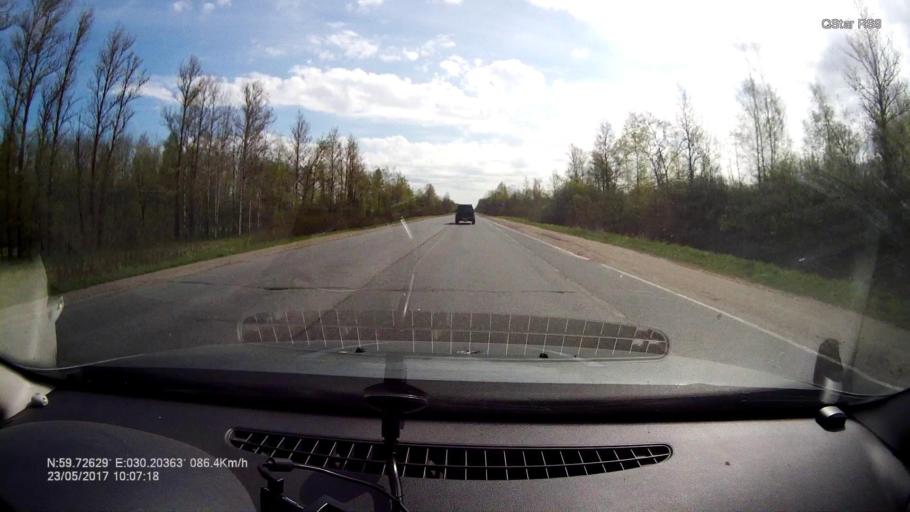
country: RU
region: St.-Petersburg
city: Gorelovo
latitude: 59.7263
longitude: 30.2044
